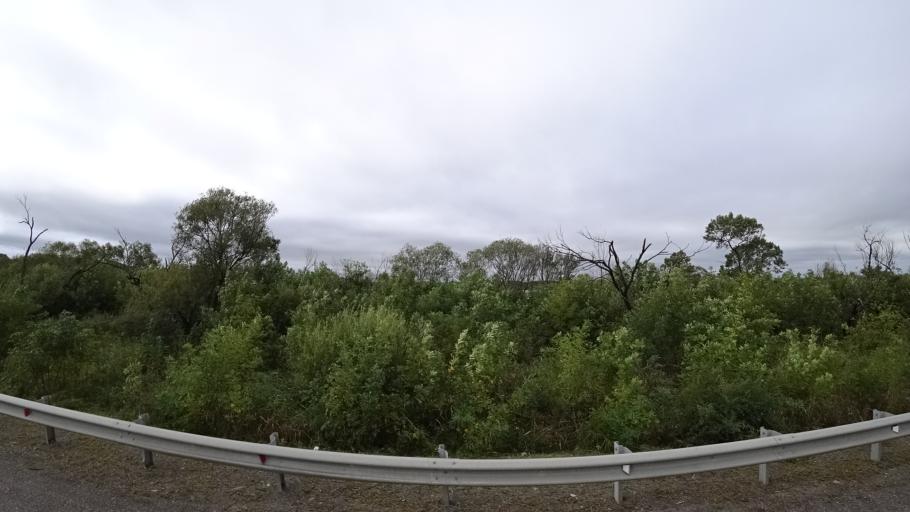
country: RU
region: Primorskiy
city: Monastyrishche
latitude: 44.1826
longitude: 132.4416
